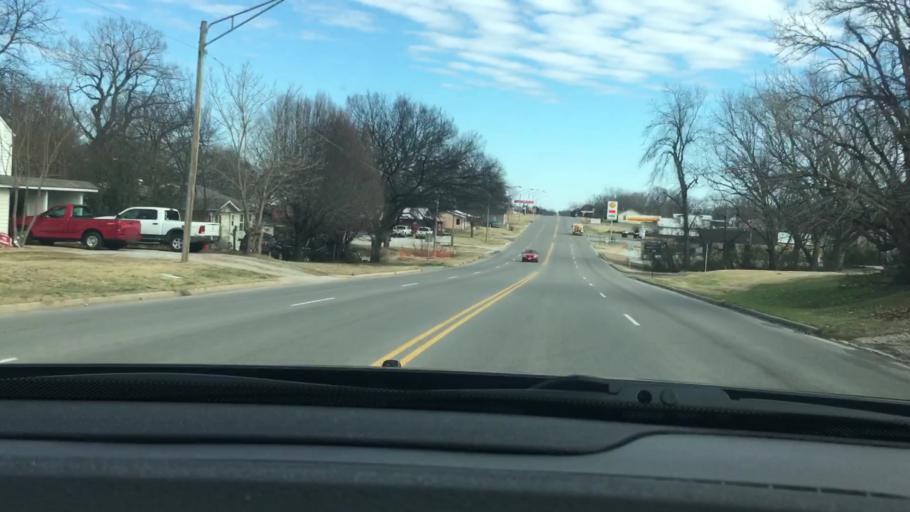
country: US
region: Oklahoma
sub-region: Garvin County
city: Stratford
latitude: 34.7967
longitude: -96.9575
